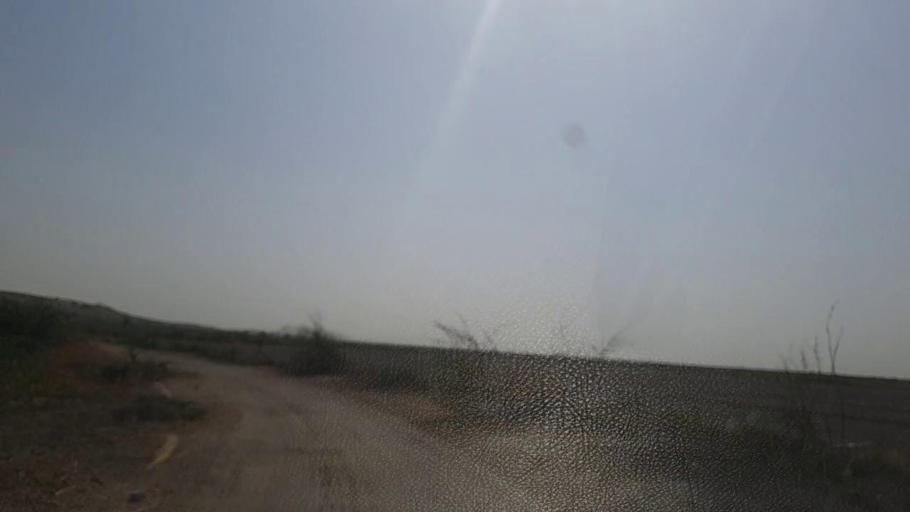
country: PK
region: Sindh
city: Naukot
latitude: 24.5948
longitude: 69.3086
